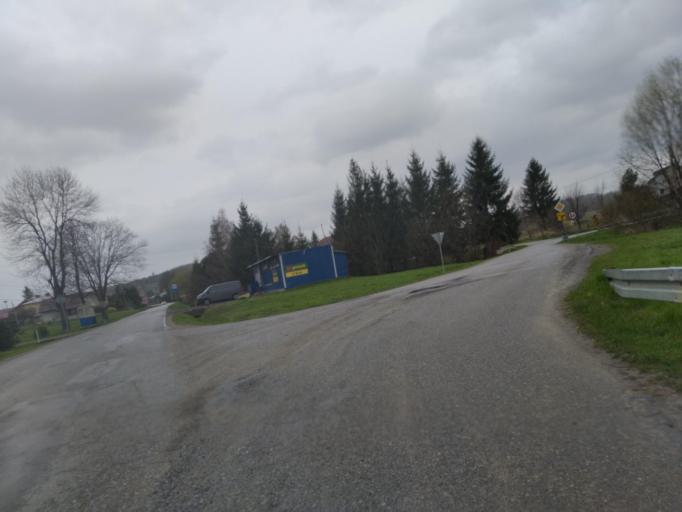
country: PL
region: Subcarpathian Voivodeship
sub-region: Powiat sanocki
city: Strachocina
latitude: 49.6102
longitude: 22.0750
